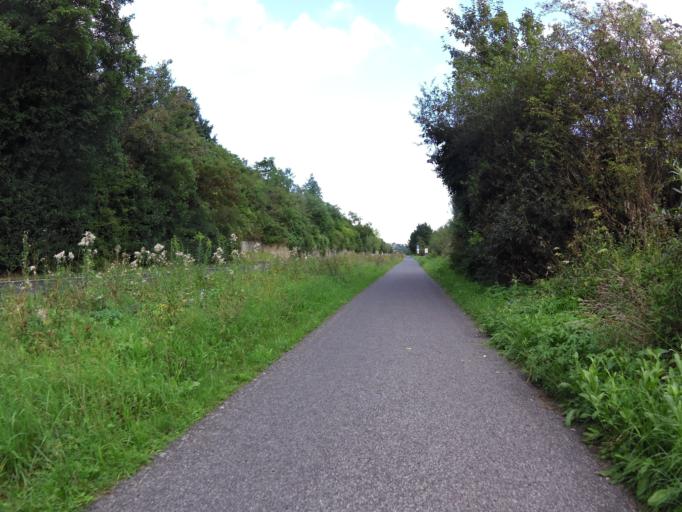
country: DE
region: Bavaria
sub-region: Regierungsbezirk Unterfranken
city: Kitzingen
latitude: 49.7492
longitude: 10.1573
